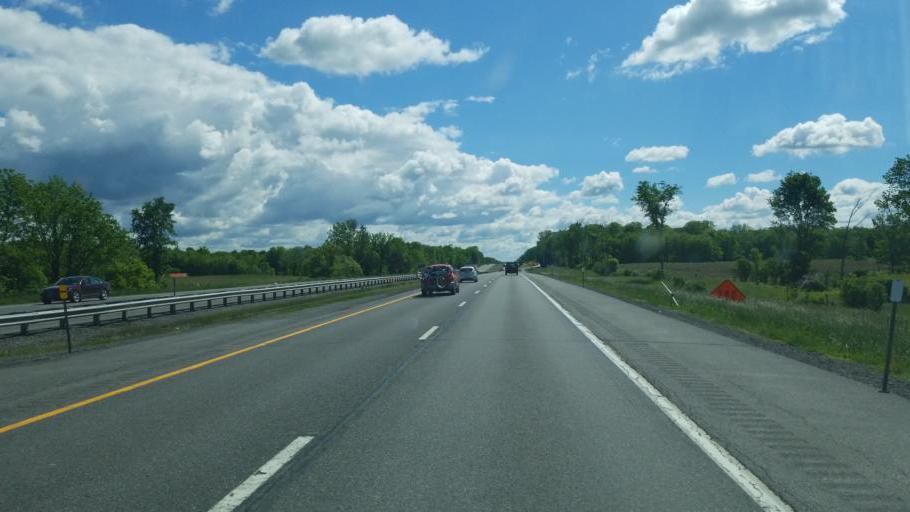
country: US
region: New York
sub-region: Oneida County
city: Vernon
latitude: 43.1289
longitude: -75.5408
